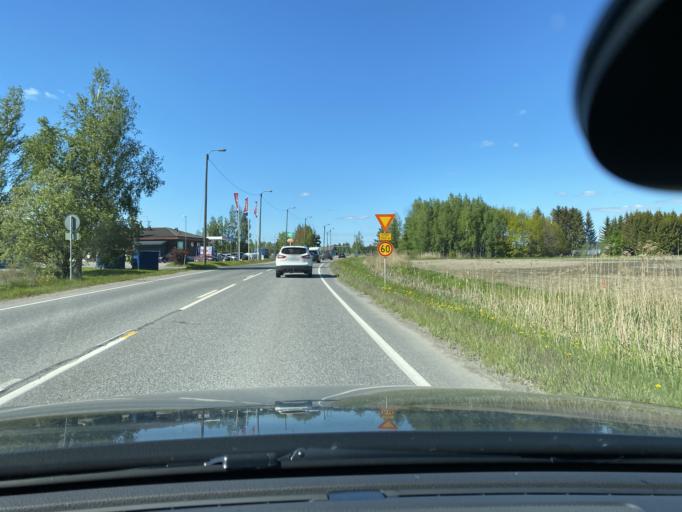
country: FI
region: Varsinais-Suomi
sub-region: Turku
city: Paimio
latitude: 60.4184
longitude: 22.6631
